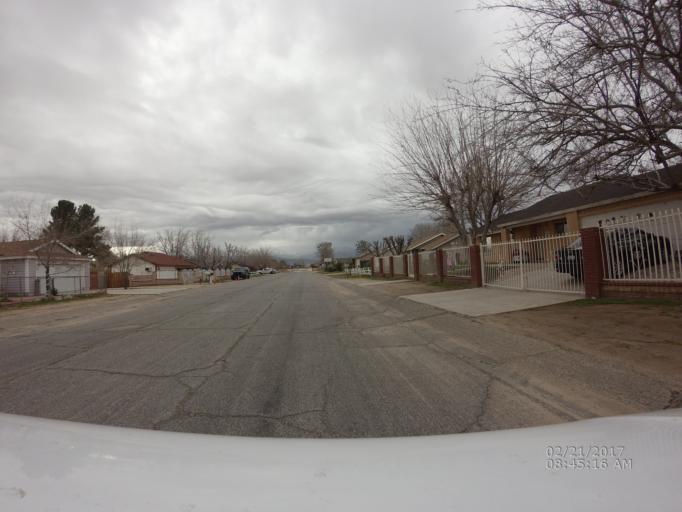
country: US
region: California
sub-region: Los Angeles County
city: Lake Los Angeles
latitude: 34.5966
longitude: -117.8313
